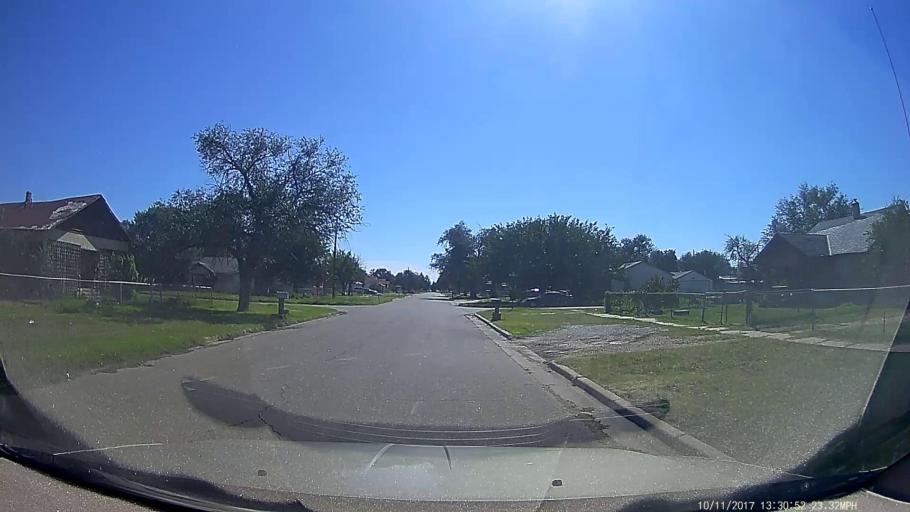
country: US
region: New Mexico
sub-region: Curry County
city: Clovis
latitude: 34.4024
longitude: -103.2117
